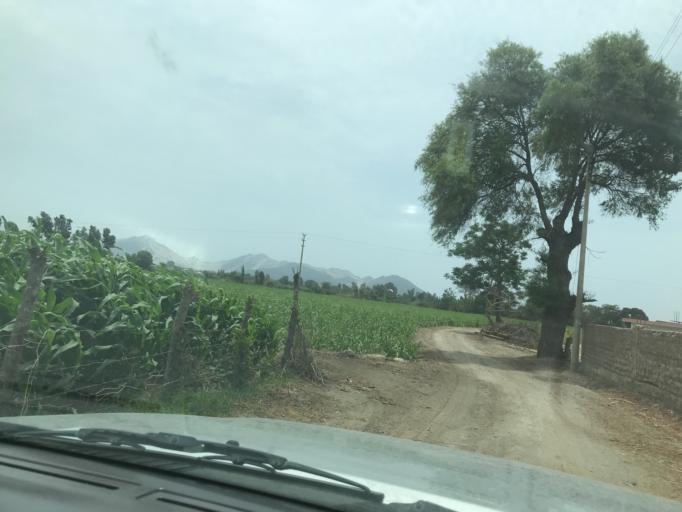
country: PE
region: La Libertad
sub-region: Viru
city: Viru
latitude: -8.4193
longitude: -78.7903
